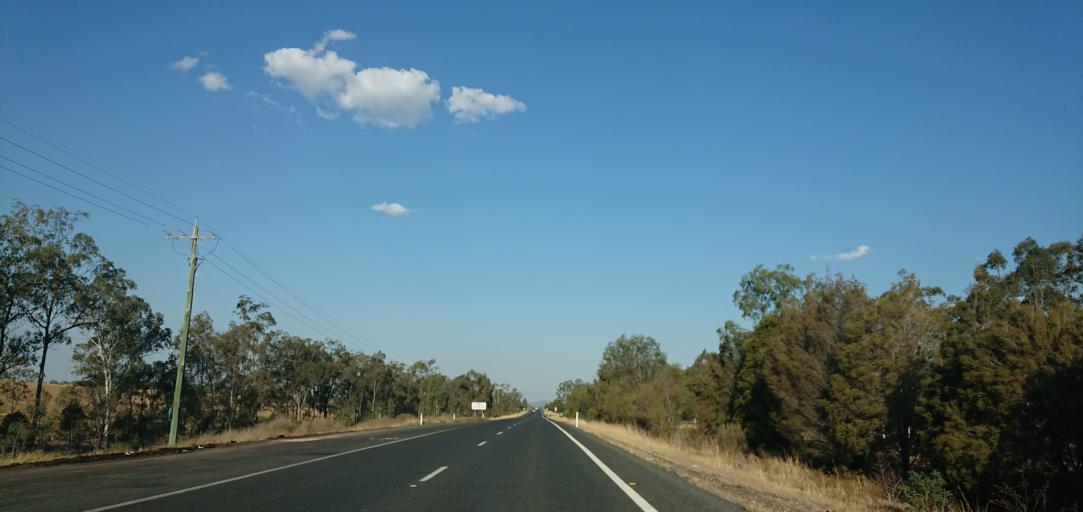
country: AU
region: Queensland
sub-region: Lockyer Valley
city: Gatton
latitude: -27.5380
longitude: 152.2778
